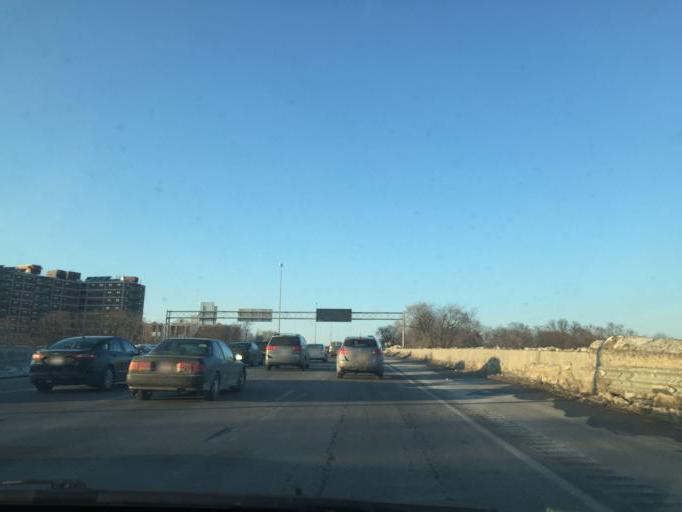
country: US
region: Massachusetts
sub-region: Middlesex County
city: Medford
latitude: 42.4142
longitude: -71.1037
